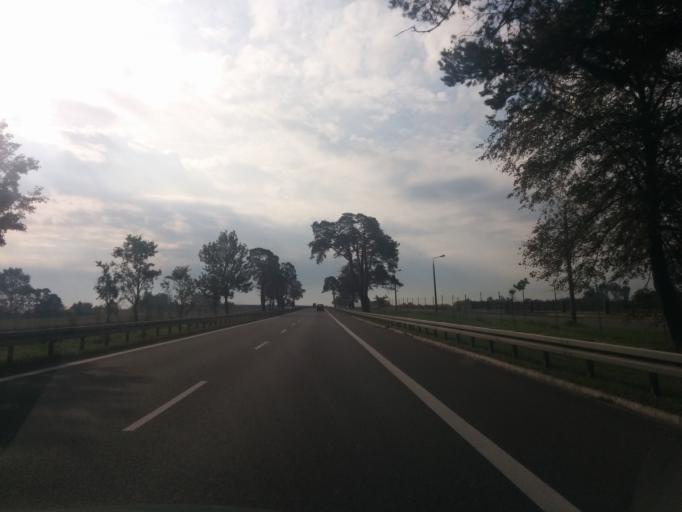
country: PL
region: Masovian Voivodeship
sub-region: Powiat bialobrzeski
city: Stara Blotnica
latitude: 51.5897
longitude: 20.9958
